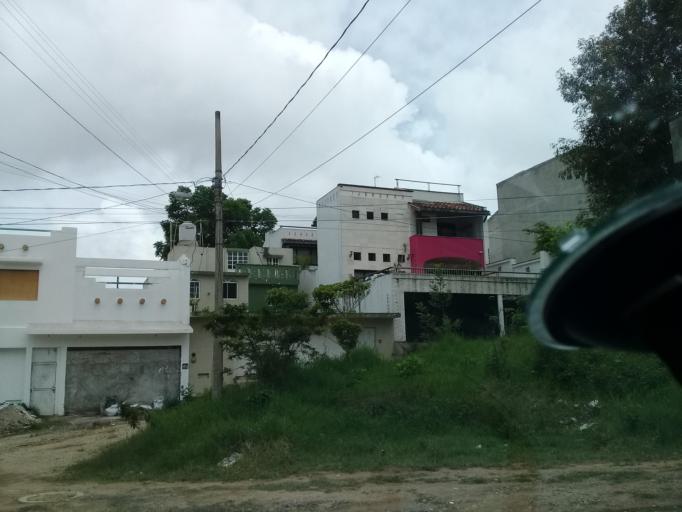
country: MX
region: Veracruz
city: El Castillo
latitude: 19.5343
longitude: -96.8842
